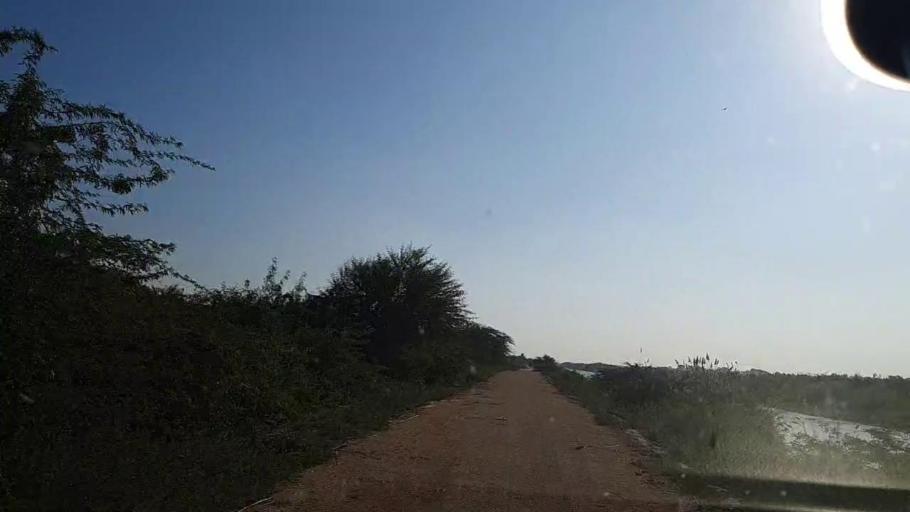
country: PK
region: Sindh
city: Chuhar Jamali
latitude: 24.5535
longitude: 68.0367
